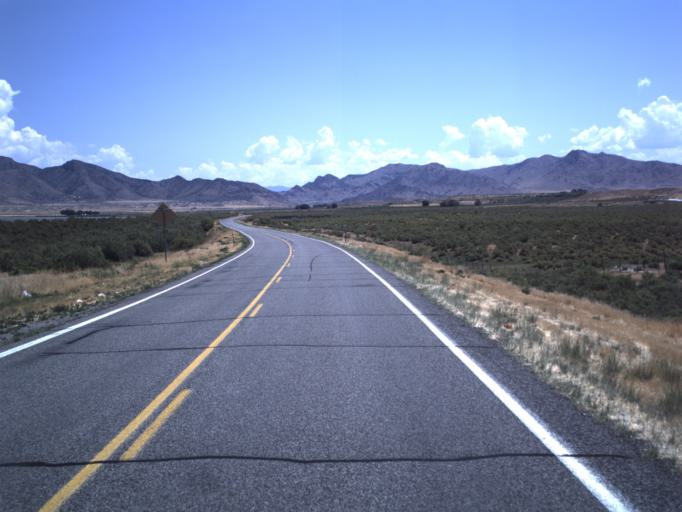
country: US
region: Utah
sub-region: Millard County
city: Delta
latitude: 39.5269
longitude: -112.3551
